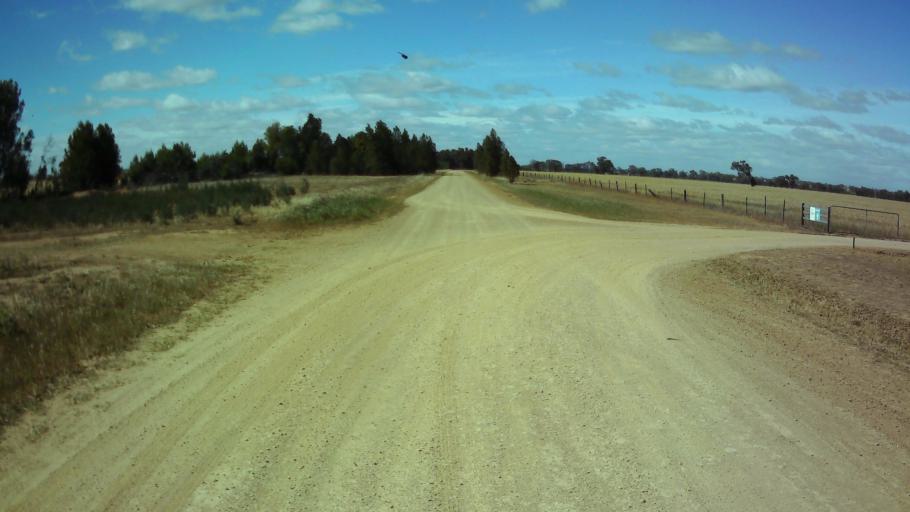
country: AU
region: New South Wales
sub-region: Weddin
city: Grenfell
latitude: -34.0305
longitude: 148.3174
